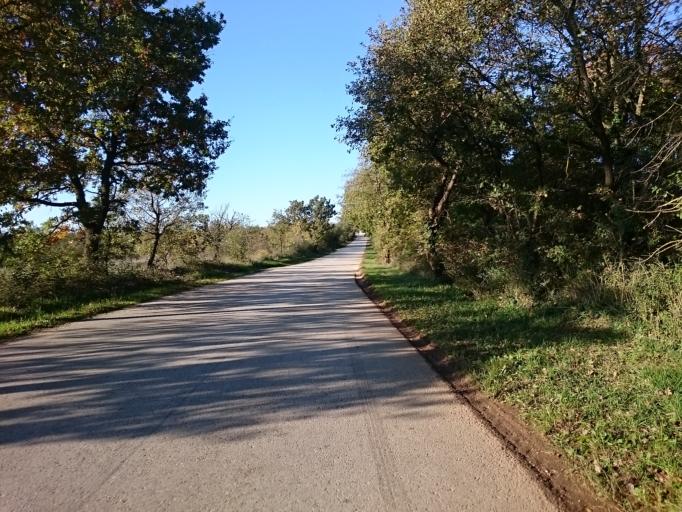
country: HR
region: Istarska
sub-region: Grad Porec
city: Porec
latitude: 45.2869
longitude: 13.6424
